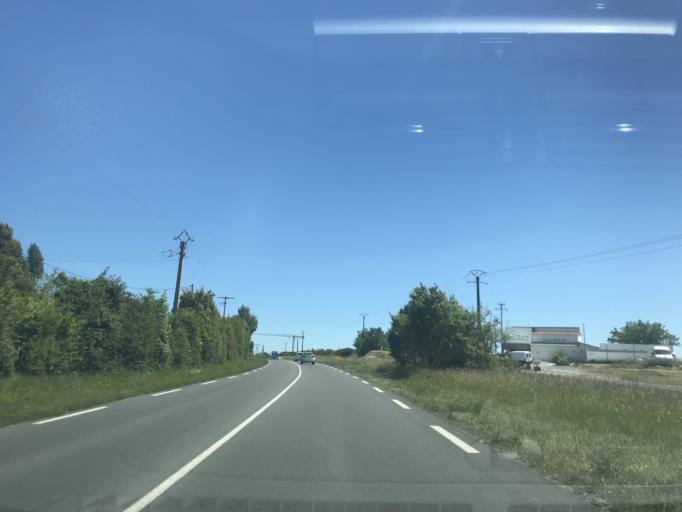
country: FR
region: Poitou-Charentes
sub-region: Departement de la Charente-Maritime
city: Vaux-sur-Mer
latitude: 45.6447
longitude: -1.0430
